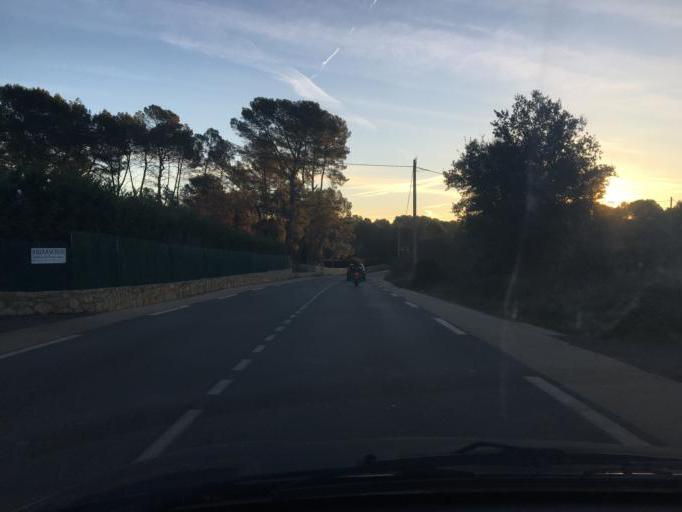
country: FR
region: Provence-Alpes-Cote d'Azur
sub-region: Departement du Var
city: Taradeau
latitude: 43.4649
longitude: 6.3962
